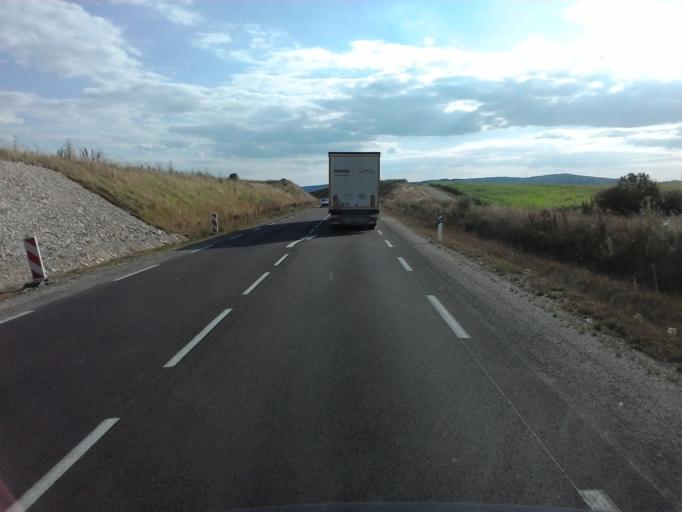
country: FR
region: Franche-Comte
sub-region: Departement de la Haute-Saone
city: Frotey-les-Vesoul
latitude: 47.6975
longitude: 6.2736
